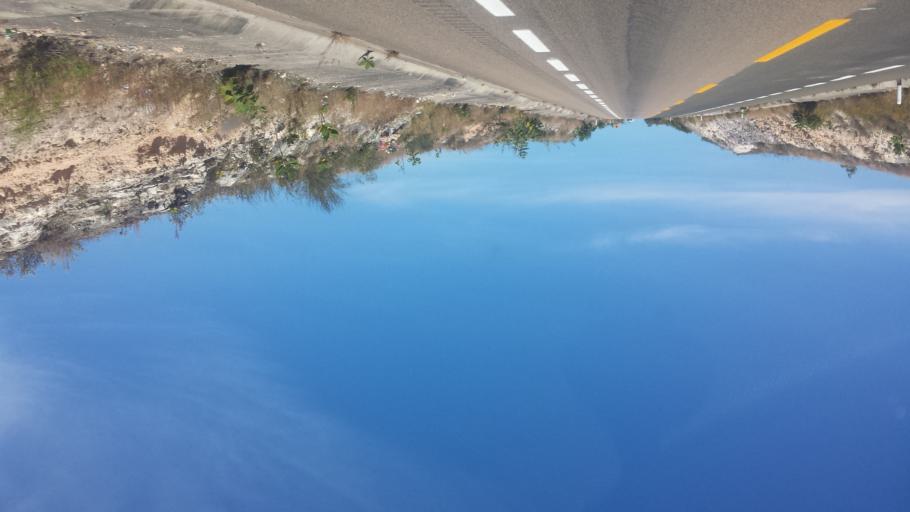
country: MX
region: Oaxaca
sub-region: Villa Tejupam de la Union
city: Villa Tejupam de la Union
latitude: 17.8042
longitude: -97.3651
